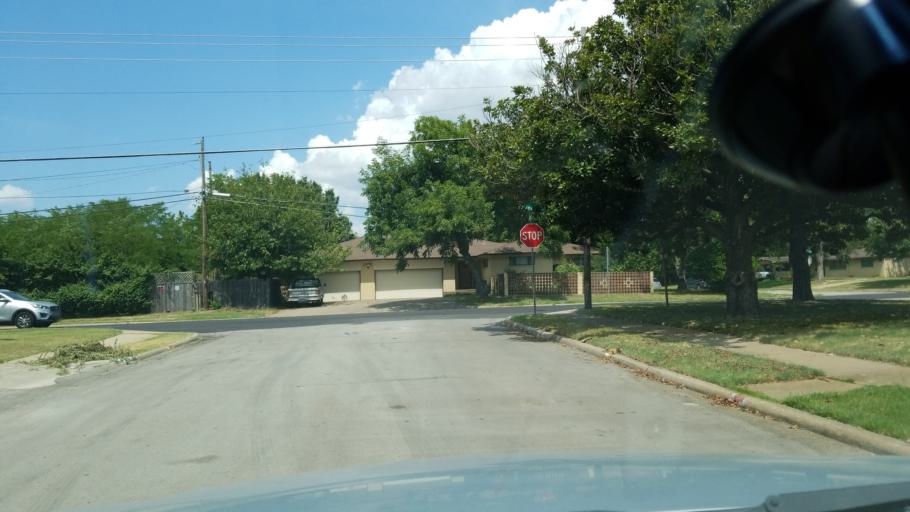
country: US
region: Texas
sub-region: Dallas County
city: Irving
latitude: 32.8250
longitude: -96.9812
